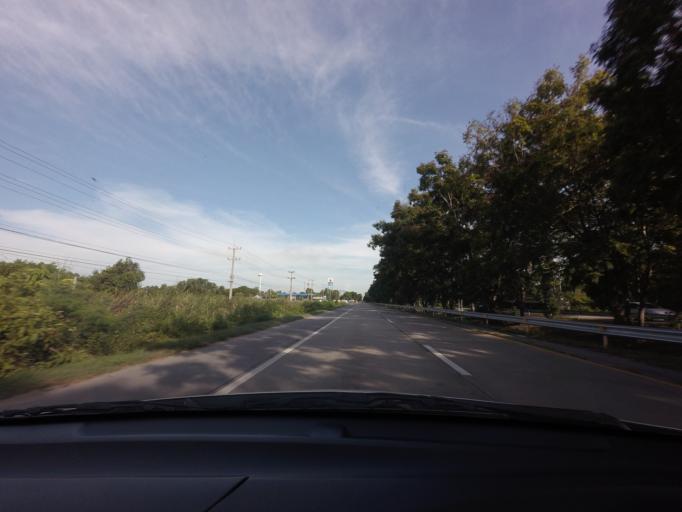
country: TH
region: Phra Nakhon Si Ayutthaya
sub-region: Amphoe Bang Sai
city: Bang Sai
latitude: 14.3145
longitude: 100.2242
